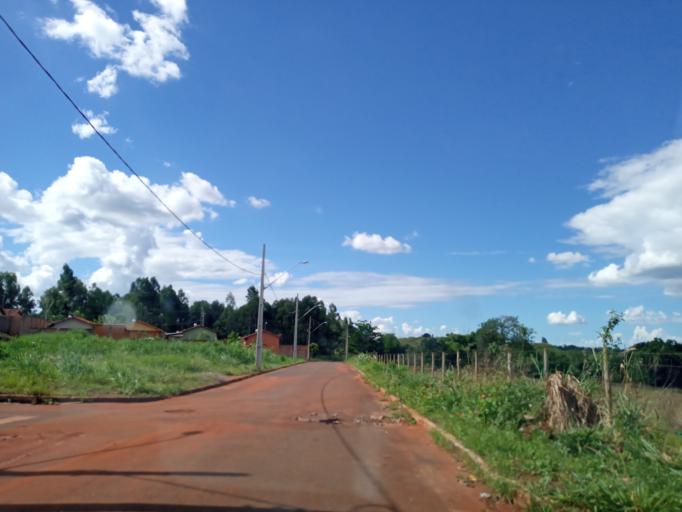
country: BR
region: Minas Gerais
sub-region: Ituiutaba
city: Ituiutaba
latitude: -18.9712
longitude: -49.4921
